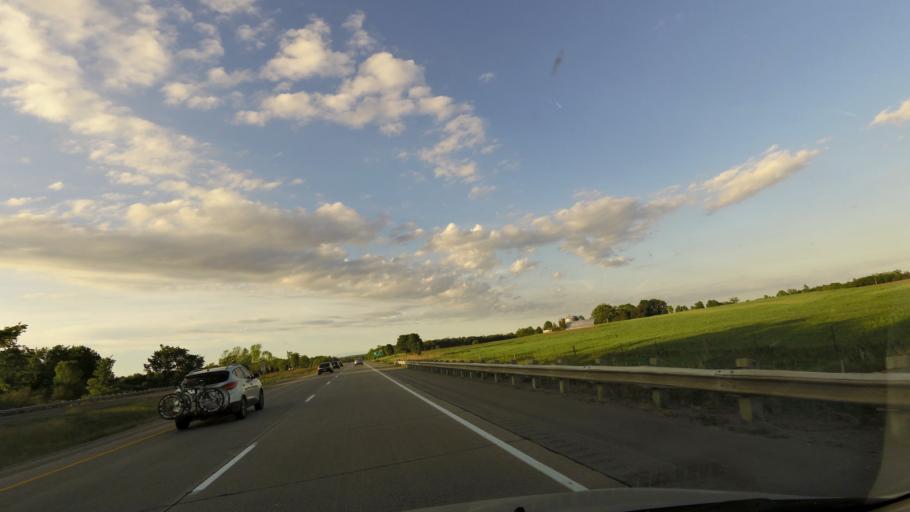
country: CA
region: Ontario
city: Omemee
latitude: 44.1918
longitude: -78.4573
